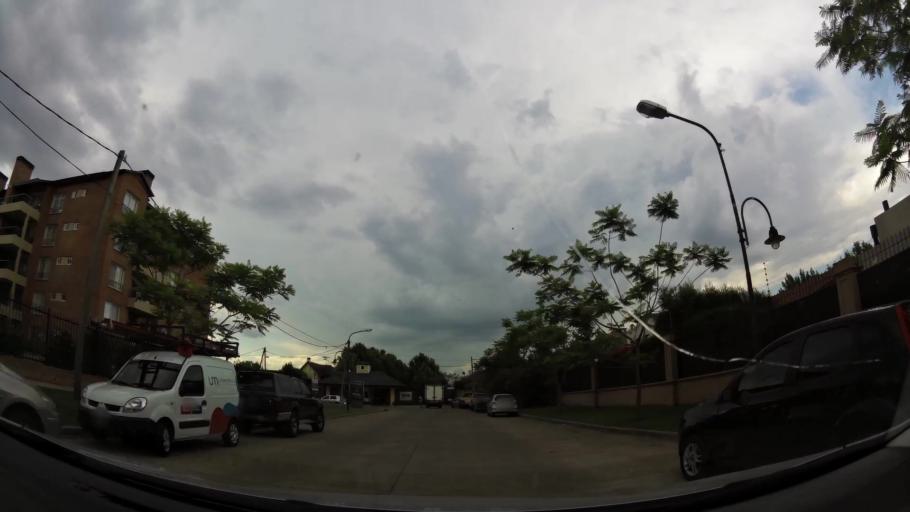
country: AR
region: Buenos Aires
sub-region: Partido de Tigre
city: Tigre
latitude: -34.4809
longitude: -58.5874
